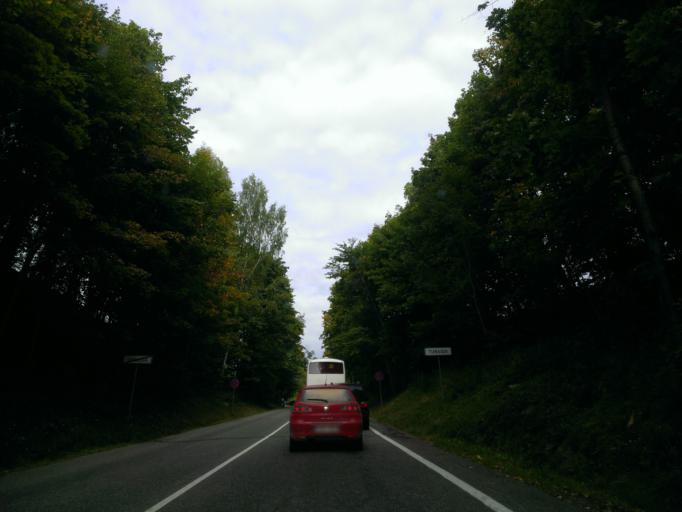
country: LV
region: Sigulda
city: Sigulda
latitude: 57.1852
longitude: 24.8471
